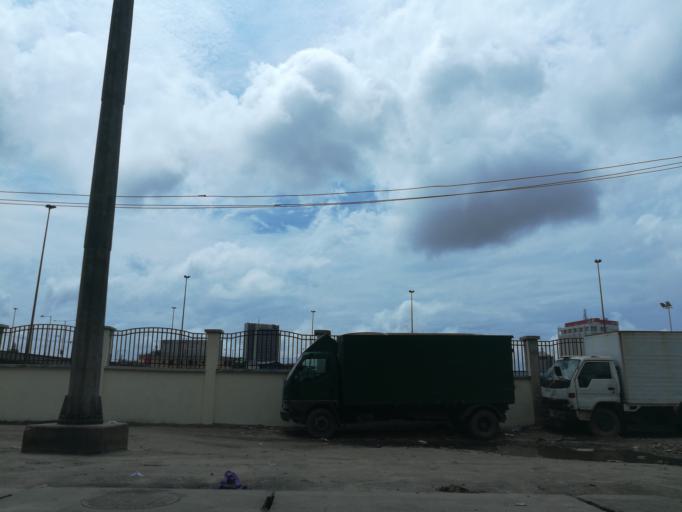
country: NG
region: Lagos
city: Lagos
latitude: 6.4616
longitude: 3.3810
